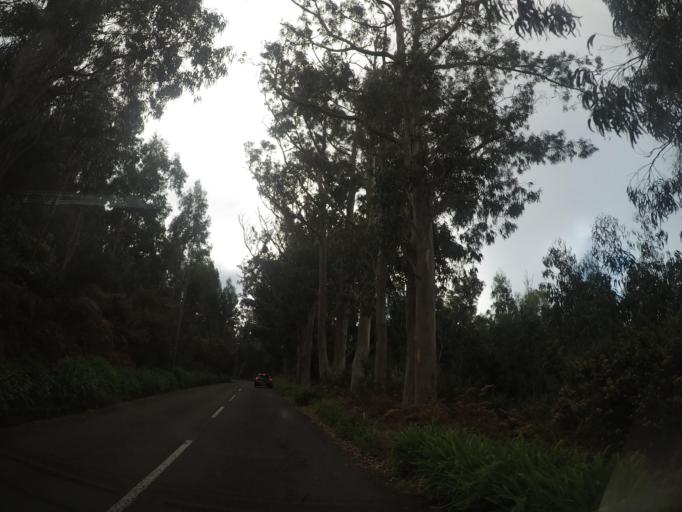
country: PT
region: Madeira
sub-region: Porto Moniz
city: Porto Moniz
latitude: 32.8391
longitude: -17.2110
